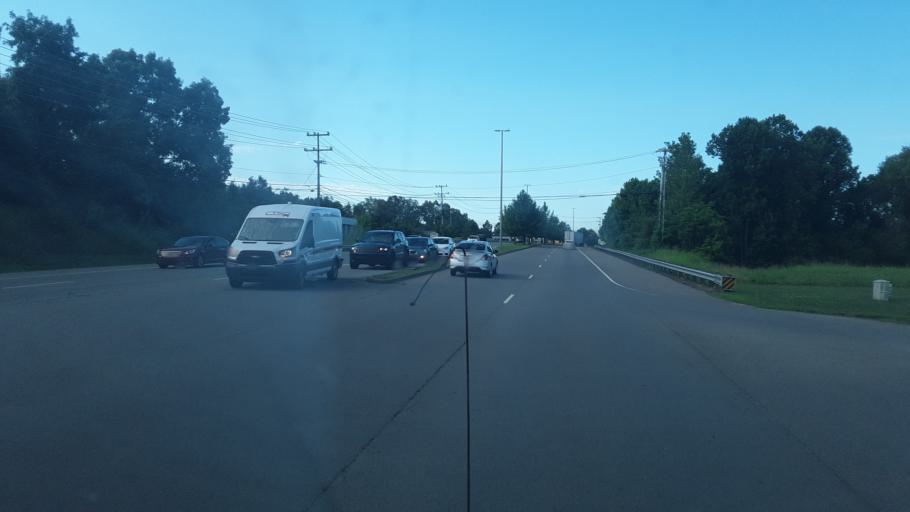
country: US
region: Tennessee
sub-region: Montgomery County
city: Clarksville
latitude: 36.5735
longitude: -87.2845
